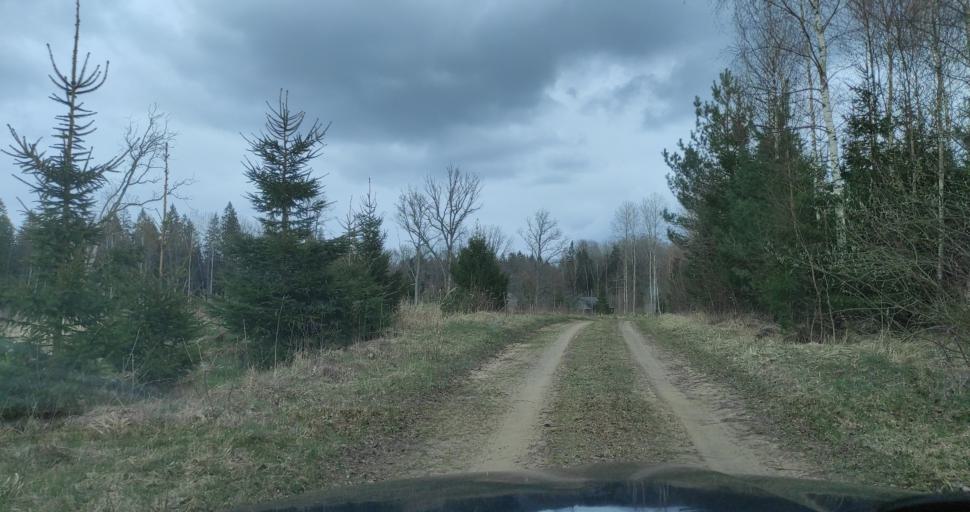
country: LV
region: Aizpute
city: Aizpute
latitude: 56.8262
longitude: 21.7644
